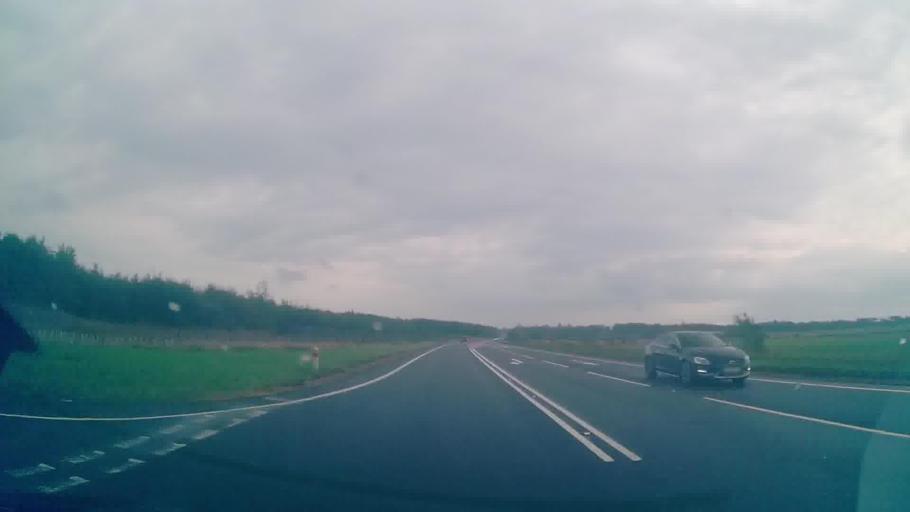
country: GB
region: Scotland
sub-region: Dumfries and Galloway
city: Lockerbie
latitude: 55.0194
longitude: -3.3658
